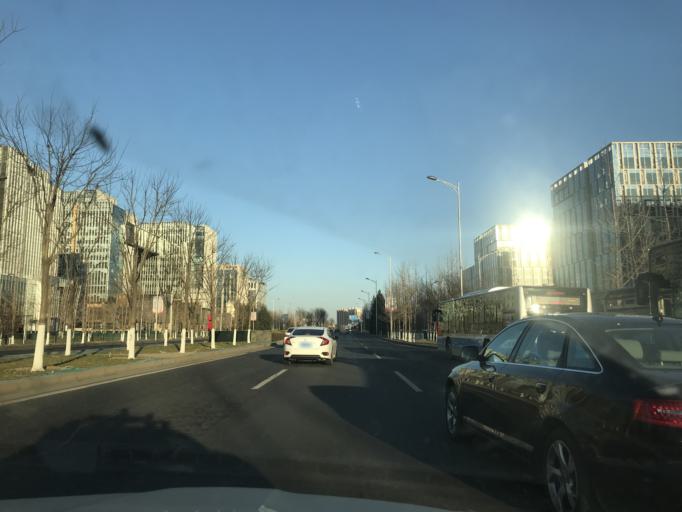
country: CN
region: Beijing
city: Xibeiwang
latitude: 40.0726
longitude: 116.2396
